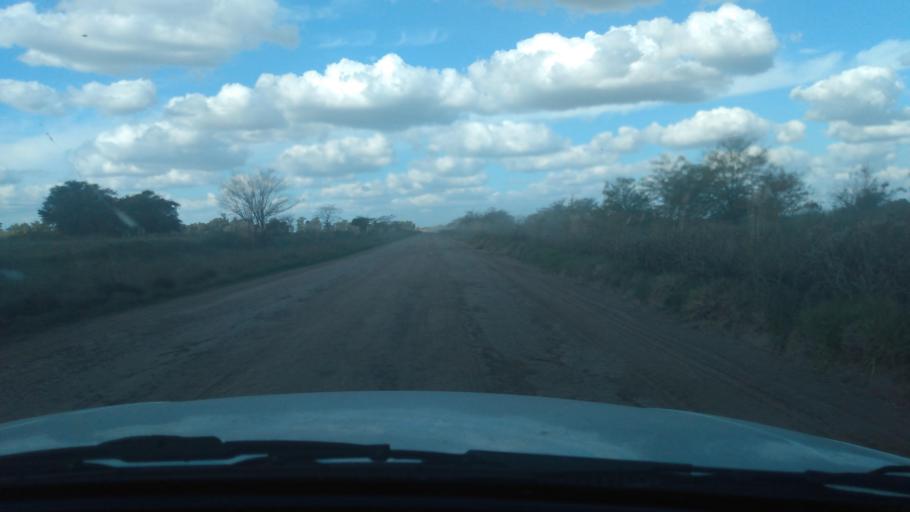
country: AR
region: Buenos Aires
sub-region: Partido de Navarro
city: Navarro
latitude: -35.0127
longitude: -59.4542
